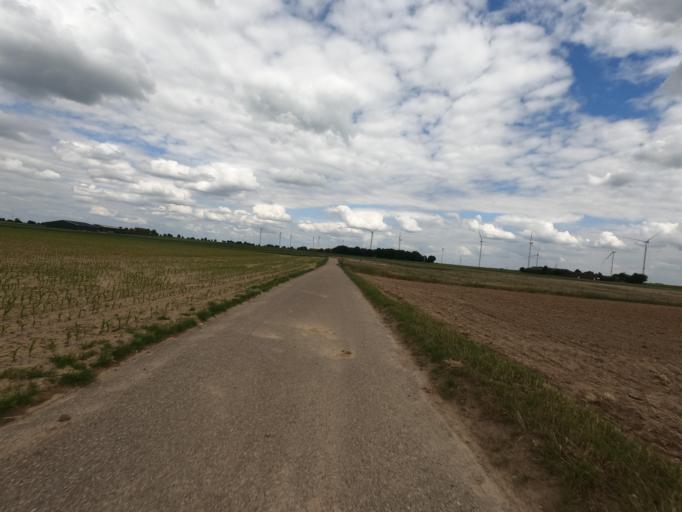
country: DE
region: North Rhine-Westphalia
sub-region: Regierungsbezirk Koln
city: Linnich
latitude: 50.9832
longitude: 6.2082
